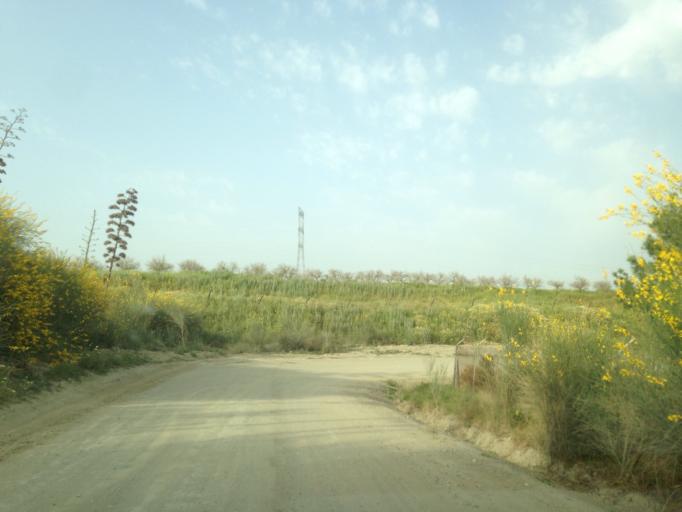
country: ES
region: Andalusia
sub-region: Provincia de Malaga
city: Estacion de Cartama
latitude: 36.7559
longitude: -4.5522
